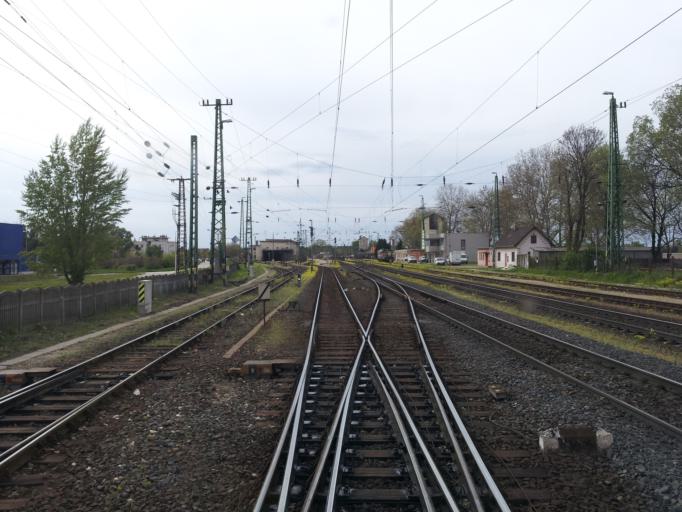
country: HU
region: Komarom-Esztergom
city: Komarom
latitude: 47.7490
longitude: 18.1189
